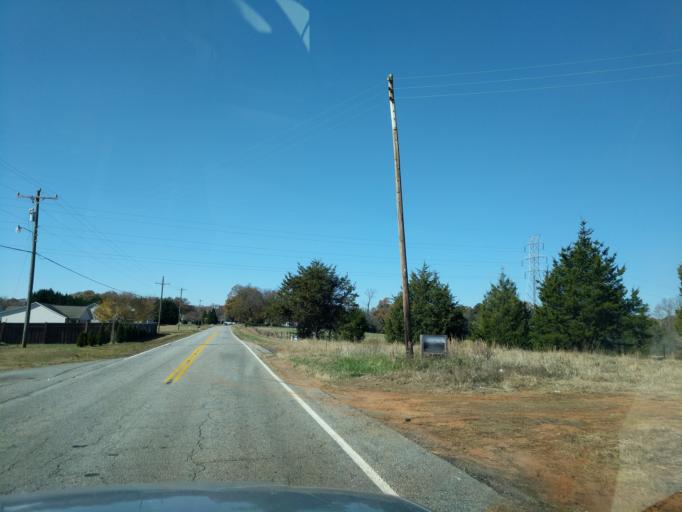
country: US
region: South Carolina
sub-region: Spartanburg County
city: Lyman
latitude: 34.9726
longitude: -82.1507
